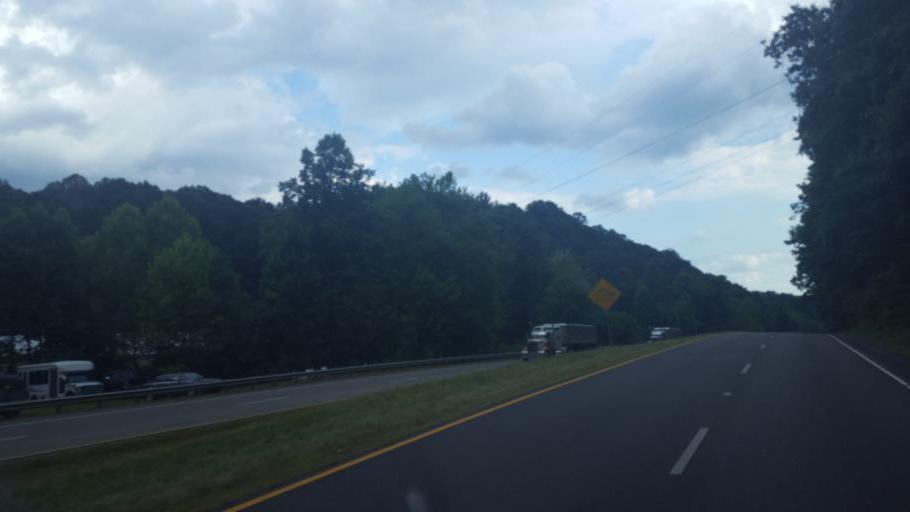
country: US
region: Virginia
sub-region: Wise County
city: Pound
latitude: 37.0825
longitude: -82.5986
